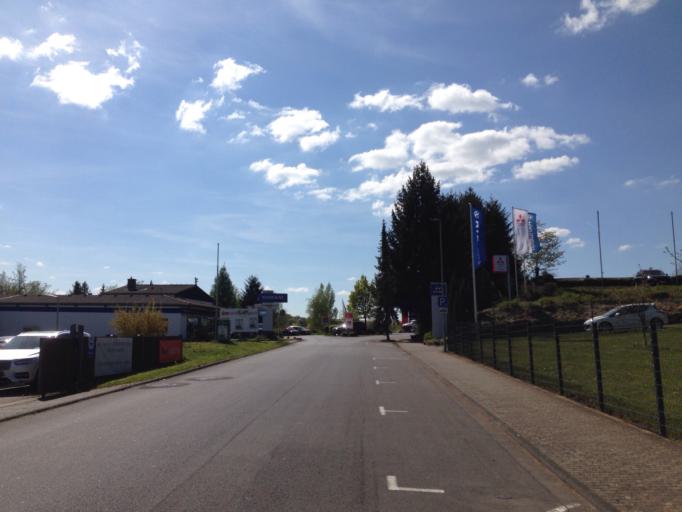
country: DE
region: Hesse
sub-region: Regierungsbezirk Giessen
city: Laubach
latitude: 50.5435
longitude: 8.9742
